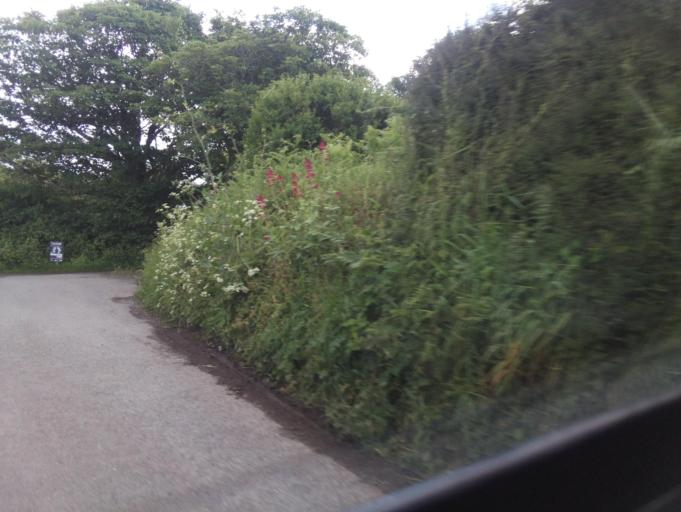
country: GB
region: England
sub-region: Devon
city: Dartmouth
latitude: 50.3541
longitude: -3.5397
